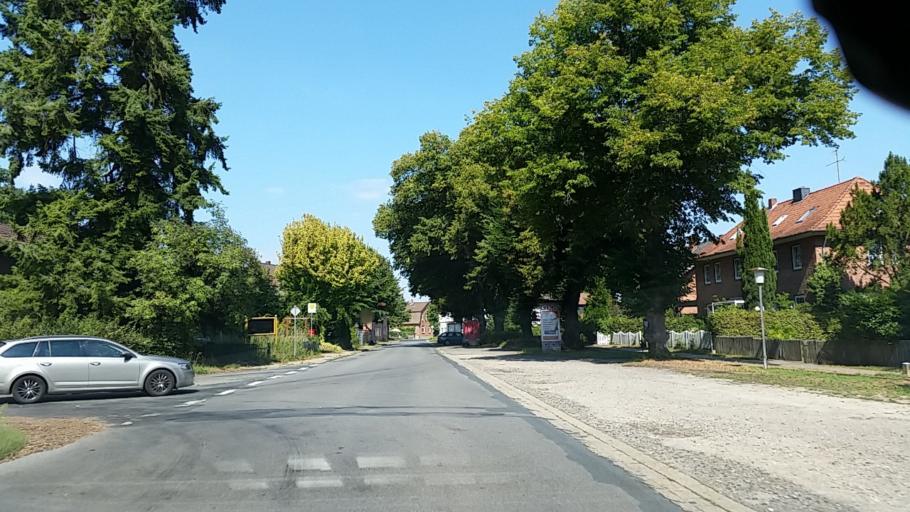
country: DE
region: Lower Saxony
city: Bad Bevensen
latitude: 53.0874
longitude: 10.5632
